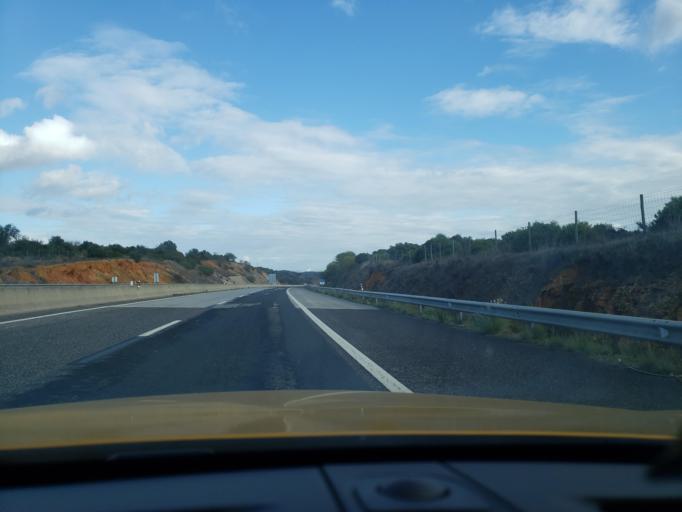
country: PT
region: Faro
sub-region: Portimao
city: Portimao
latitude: 37.1780
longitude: -8.5546
